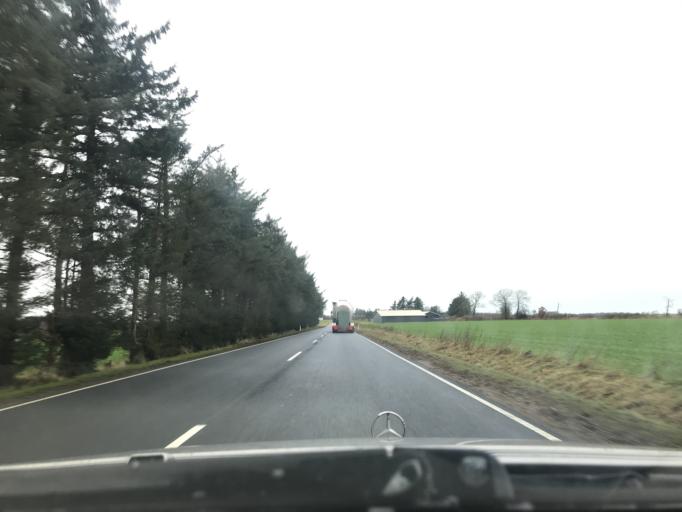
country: DK
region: South Denmark
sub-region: Esbjerg Kommune
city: Ribe
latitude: 55.2807
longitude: 8.8524
